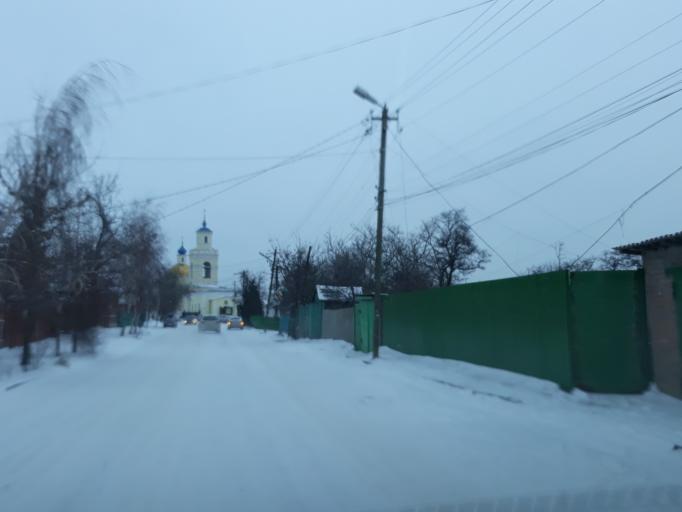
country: RU
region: Rostov
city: Taganrog
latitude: 47.2014
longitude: 38.9376
